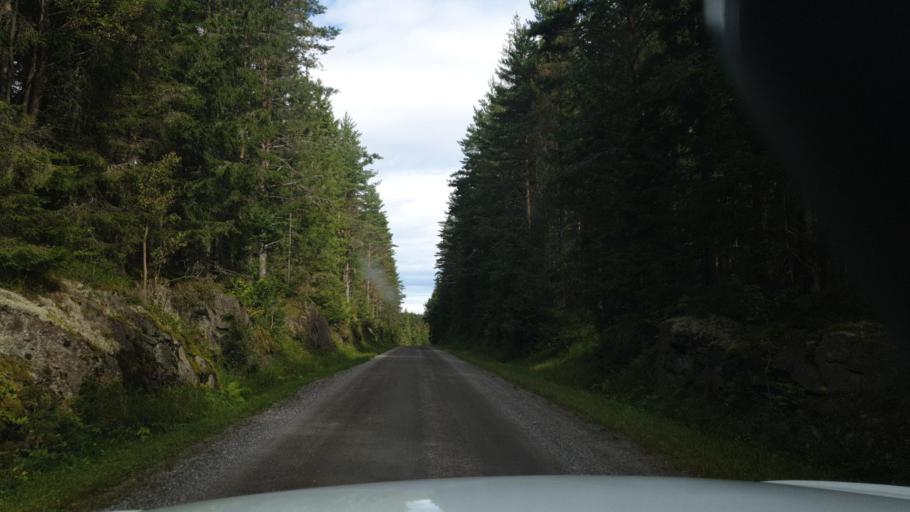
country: SE
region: Vaermland
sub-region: Eda Kommun
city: Charlottenberg
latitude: 60.0120
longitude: 12.5056
